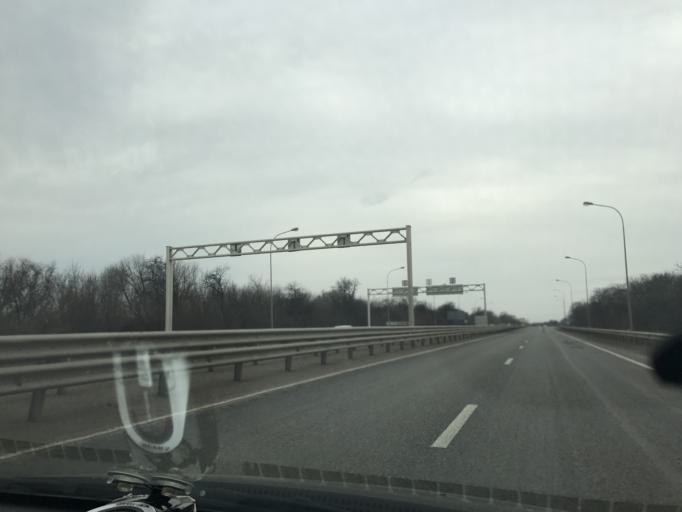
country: RU
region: Stavropol'skiy
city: Barsukovskaya
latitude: 44.7137
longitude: 41.8091
